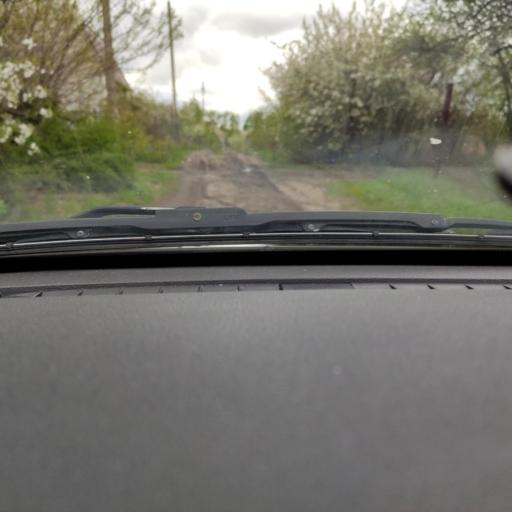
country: RU
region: Voronezj
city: Maslovka
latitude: 51.4940
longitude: 39.2119
